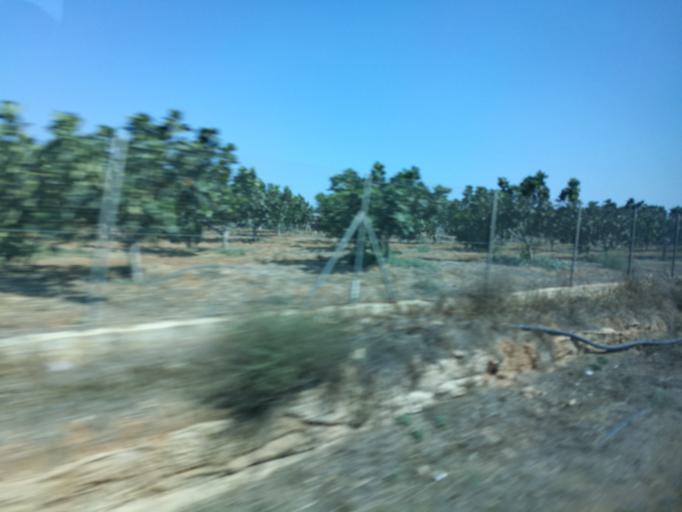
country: CY
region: Ammochostos
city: Achna
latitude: 35.0525
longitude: 33.7935
